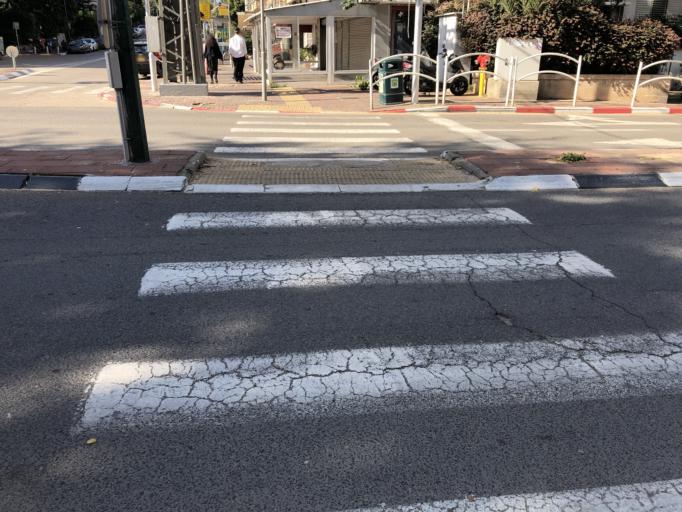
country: IL
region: Tel Aviv
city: Bene Beraq
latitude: 32.0792
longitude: 34.8255
